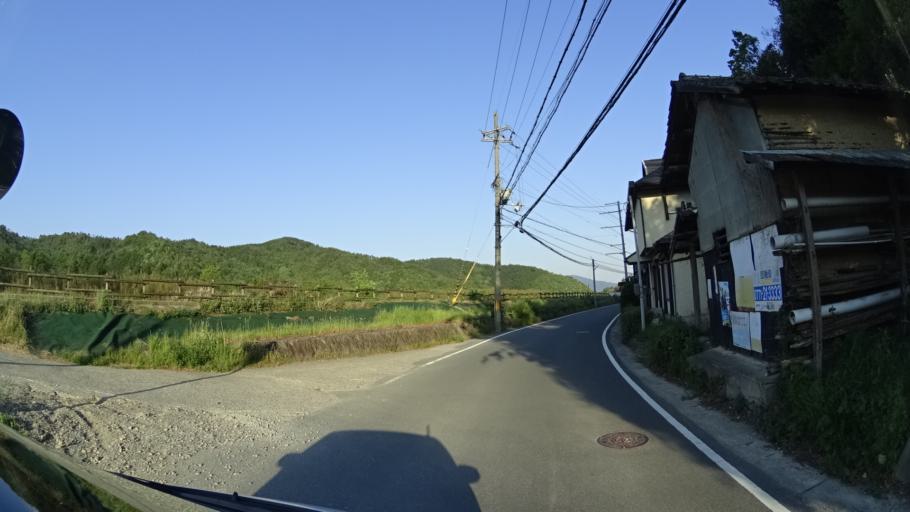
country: JP
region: Kyoto
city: Kameoka
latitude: 35.0876
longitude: 135.5130
